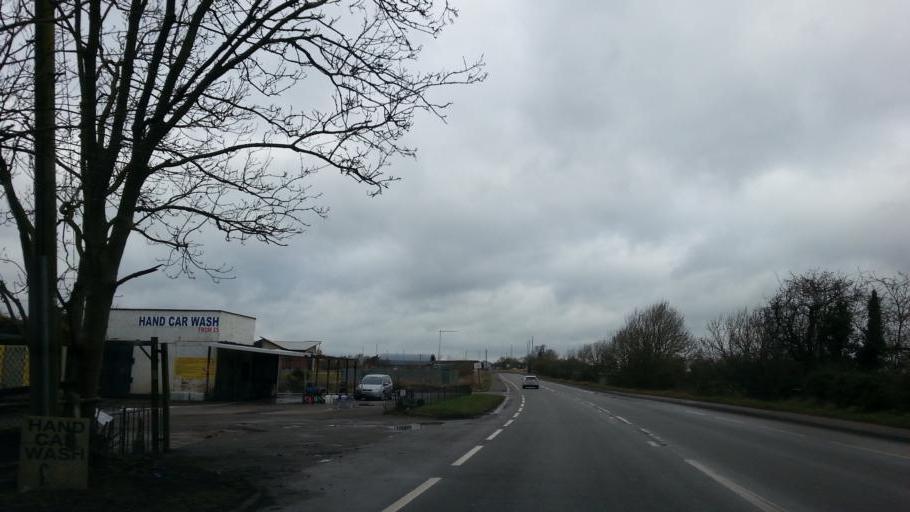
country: GB
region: England
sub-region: Leicestershire
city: Market Harborough
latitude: 52.4928
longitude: -0.9362
